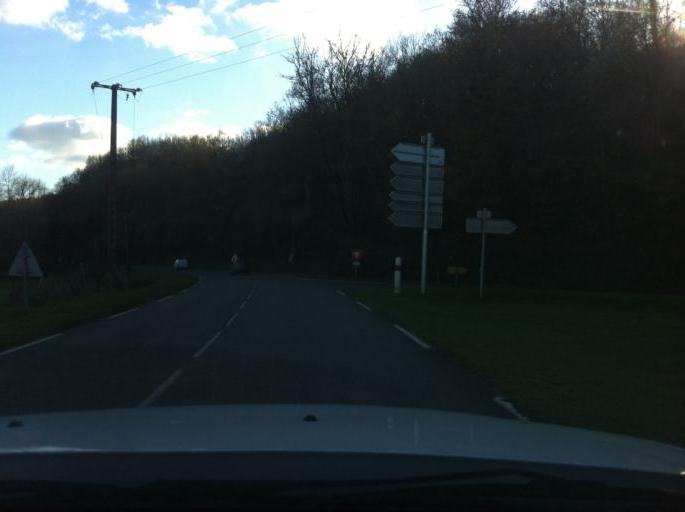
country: FR
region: Aquitaine
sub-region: Departement de la Dordogne
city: Rouffignac-Saint-Cernin-de-Reilhac
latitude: 45.0123
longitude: 0.9223
